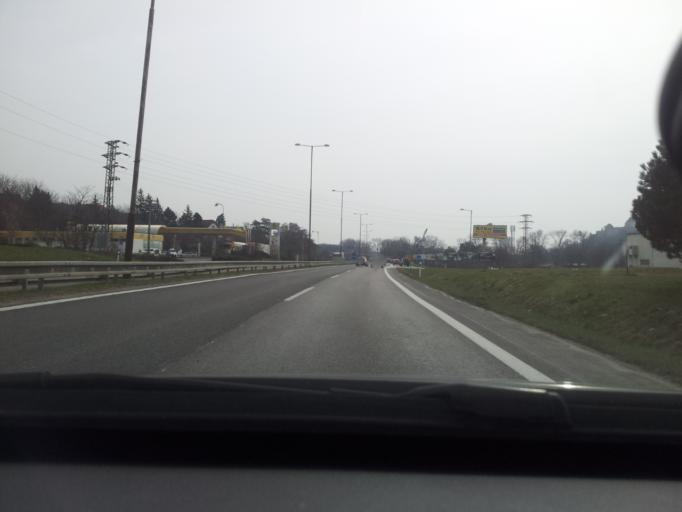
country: SK
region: Nitriansky
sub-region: Okres Nitra
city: Nitra
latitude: 48.3275
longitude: 18.0833
